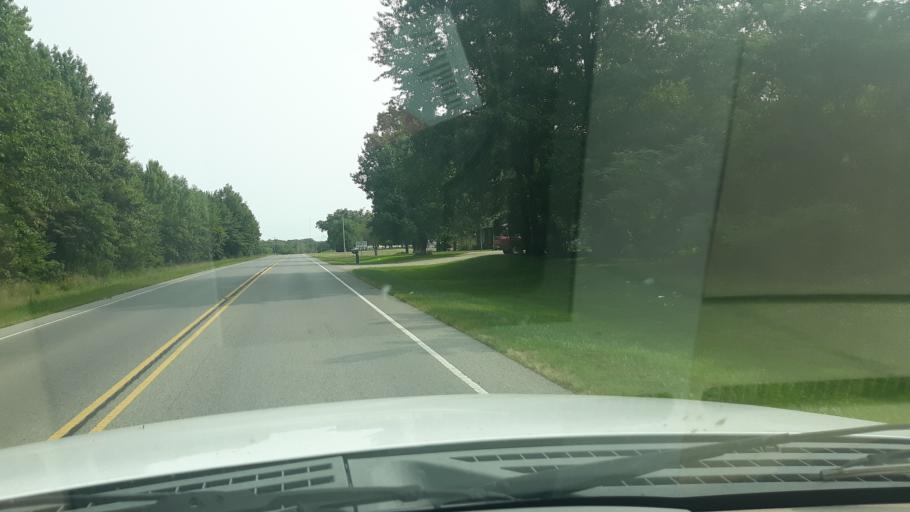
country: US
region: Illinois
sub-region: White County
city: Carmi
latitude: 38.0692
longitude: -88.2115
